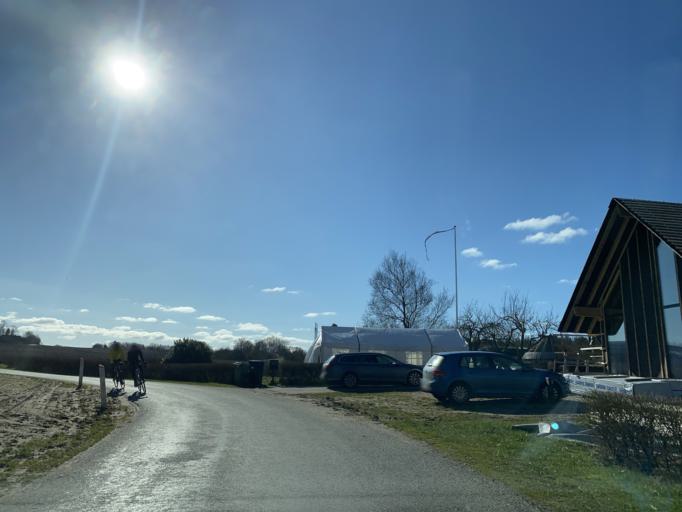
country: DK
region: Central Jutland
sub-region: Arhus Kommune
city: Sabro
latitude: 56.1791
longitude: 10.0404
